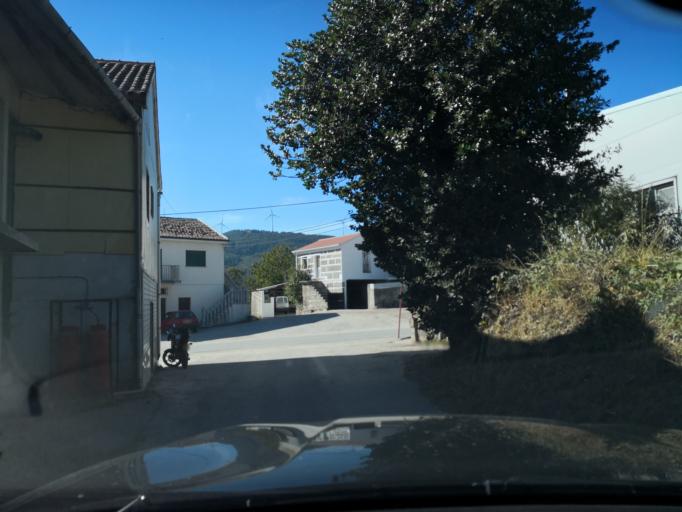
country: PT
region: Vila Real
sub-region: Santa Marta de Penaguiao
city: Santa Marta de Penaguiao
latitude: 41.3012
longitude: -7.8705
